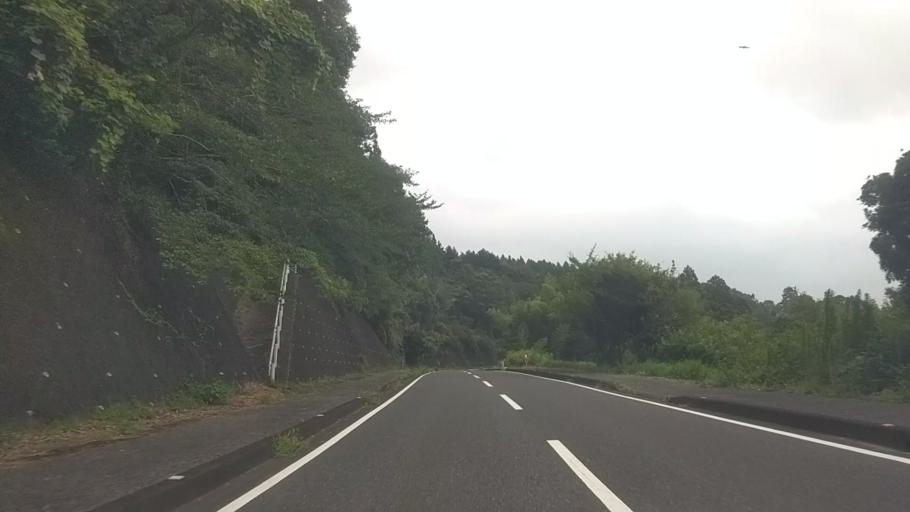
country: JP
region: Chiba
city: Kawaguchi
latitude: 35.2397
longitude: 140.0844
